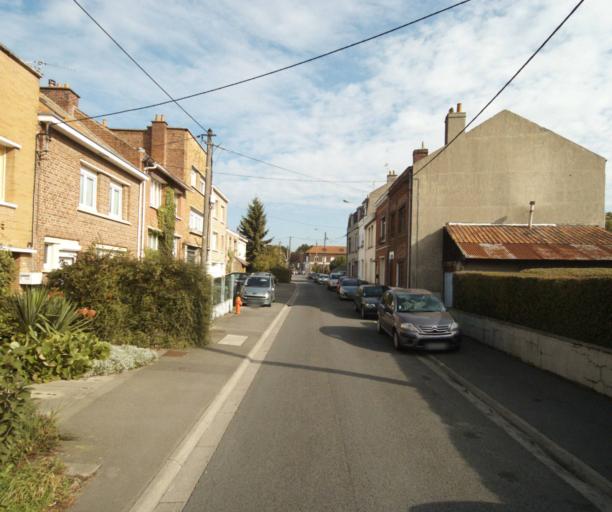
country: FR
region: Nord-Pas-de-Calais
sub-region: Departement du Nord
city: Wattignies
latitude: 50.5819
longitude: 3.0363
